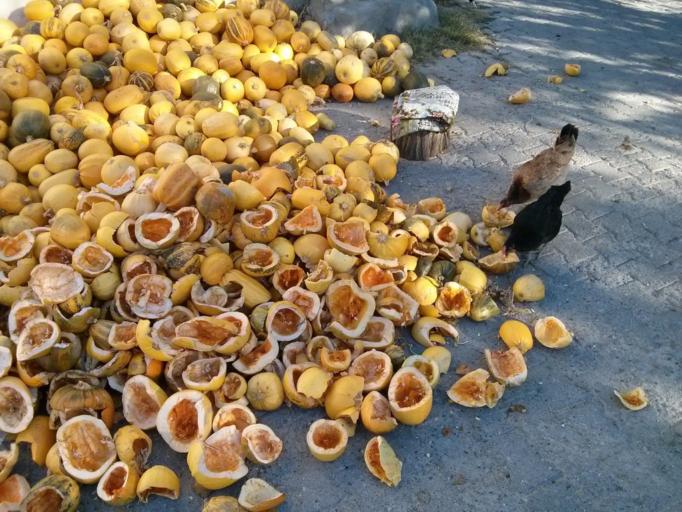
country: TR
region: Nevsehir
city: Goereme
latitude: 38.6399
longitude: 34.8292
